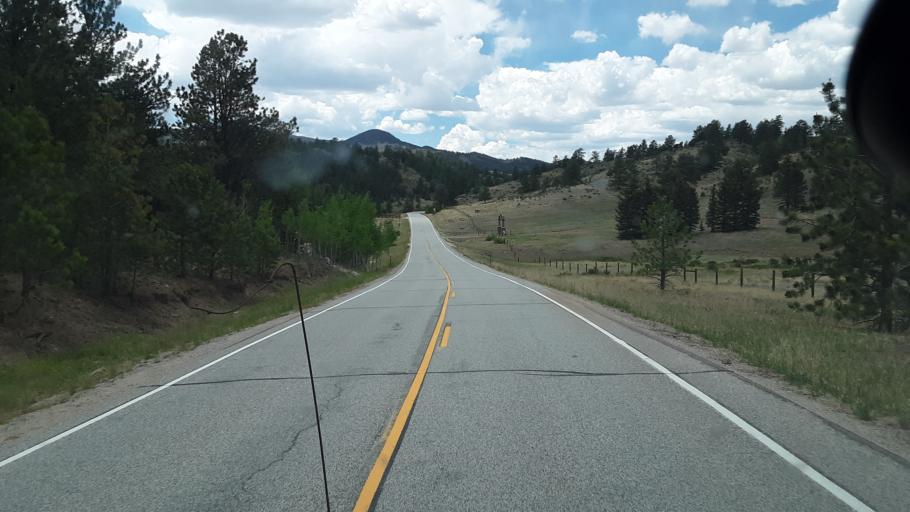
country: US
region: Colorado
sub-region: Teller County
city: Cripple Creek
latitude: 38.7835
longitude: -105.5762
